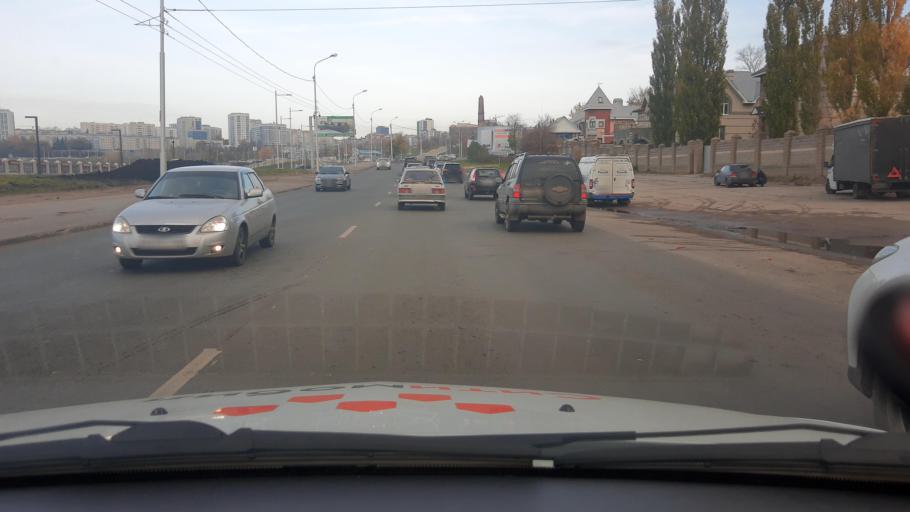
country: RU
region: Bashkortostan
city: Ufa
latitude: 54.7073
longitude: 55.9658
